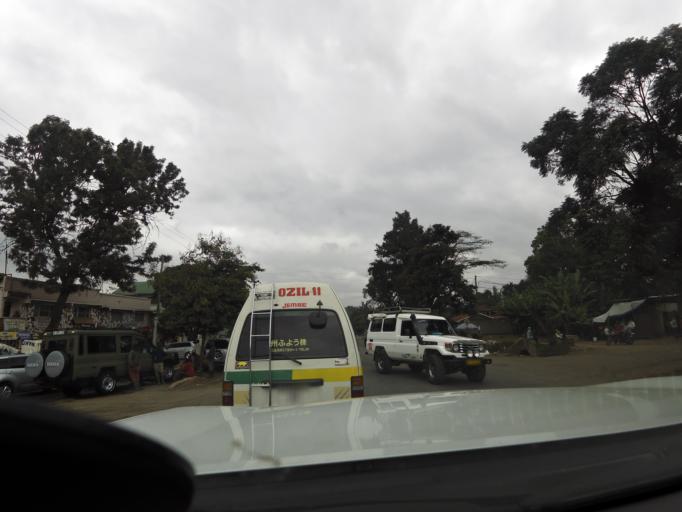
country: TZ
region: Arusha
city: Arusha
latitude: -3.3625
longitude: 36.6684
